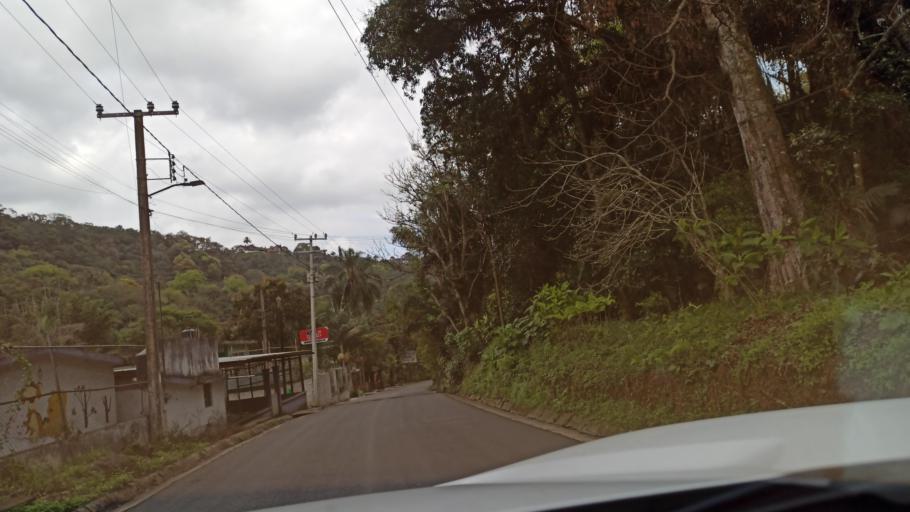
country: MX
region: Veracruz
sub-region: Fortin
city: Fortin de las Flores
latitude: 18.8928
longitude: -97.0080
